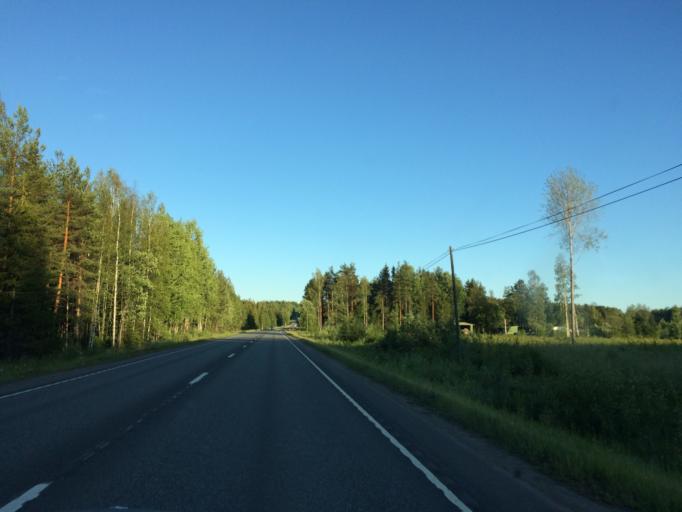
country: FI
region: Haeme
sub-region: Riihimaeki
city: Riihimaeki
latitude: 60.7730
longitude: 24.7008
